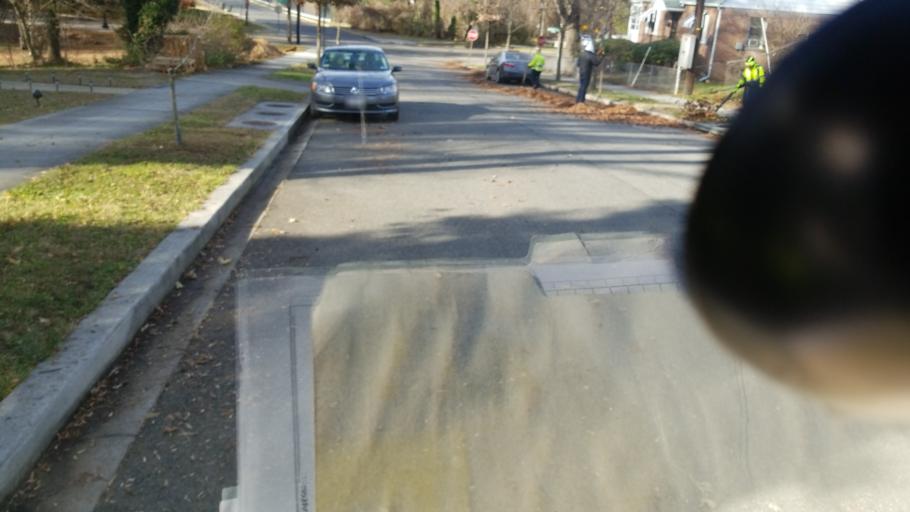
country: US
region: Maryland
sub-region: Prince George's County
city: Silver Hill
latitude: 38.8757
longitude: -76.9603
